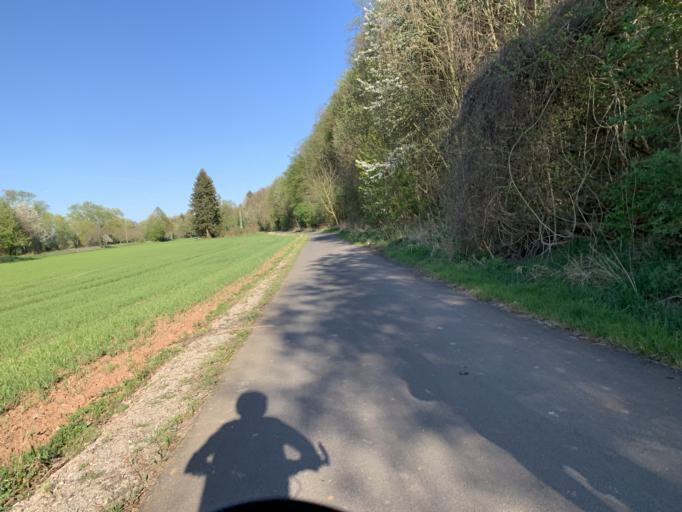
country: DE
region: Rheinland-Pfalz
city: Dorsheim
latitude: 49.8871
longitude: 7.8665
